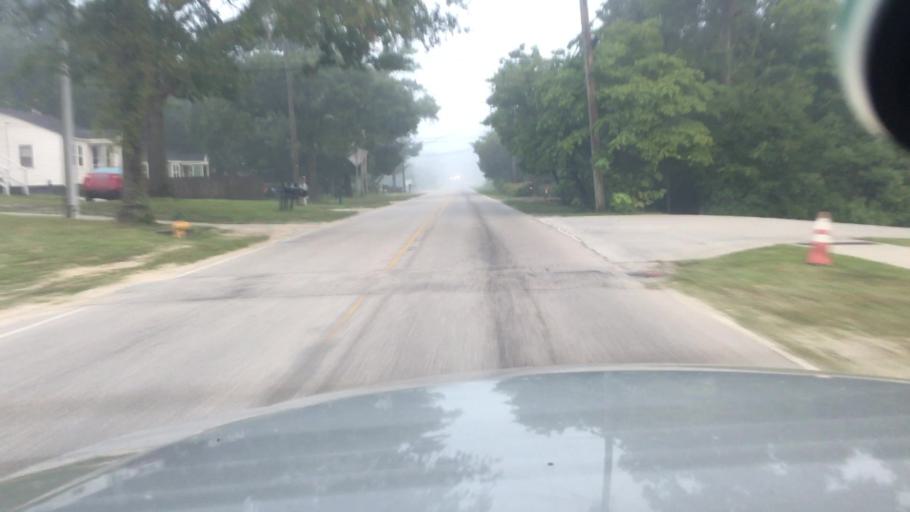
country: US
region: North Carolina
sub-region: Cumberland County
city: Fayetteville
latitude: 35.0135
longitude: -78.8991
